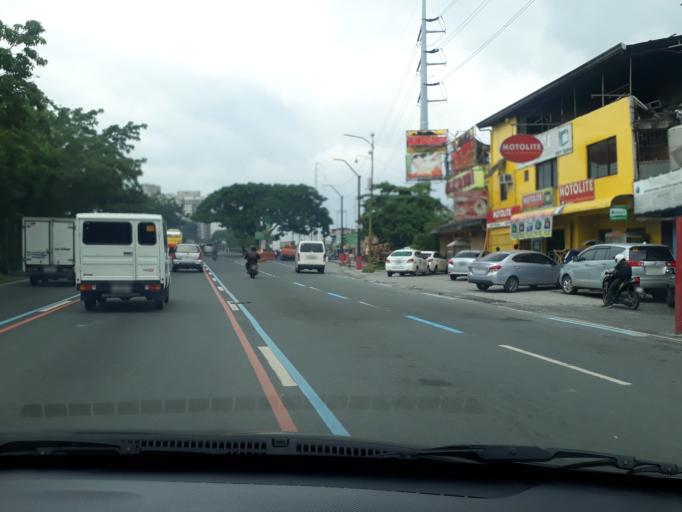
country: PH
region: Calabarzon
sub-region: Province of Rizal
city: Pateros
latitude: 14.5349
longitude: 121.0575
